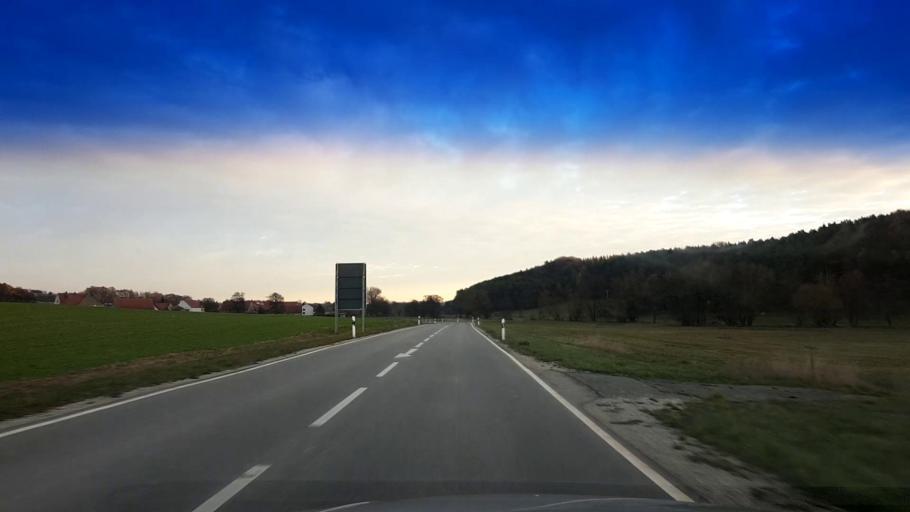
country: DE
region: Bavaria
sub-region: Upper Franconia
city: Priesendorf
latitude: 49.8893
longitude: 10.7403
